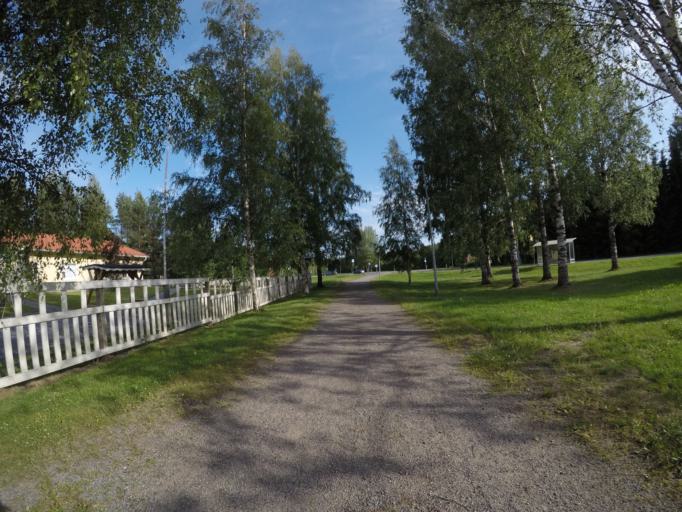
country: FI
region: Haeme
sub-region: Haemeenlinna
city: Haemeenlinna
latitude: 60.9775
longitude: 24.4345
